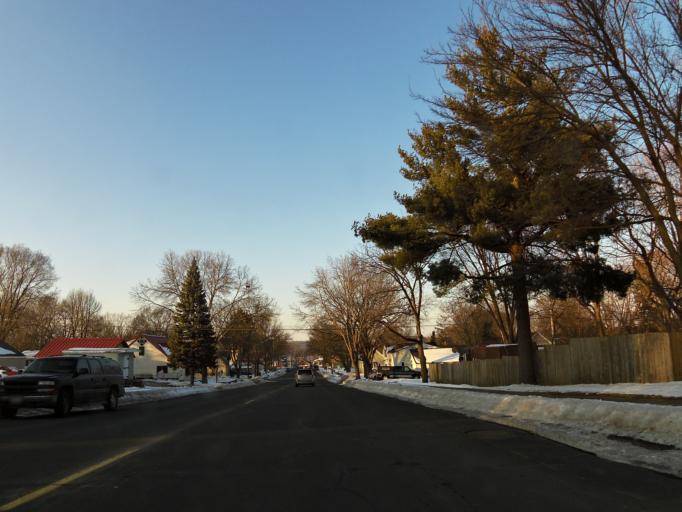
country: US
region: Minnesota
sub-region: Scott County
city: Shakopee
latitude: 44.7961
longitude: -93.5217
